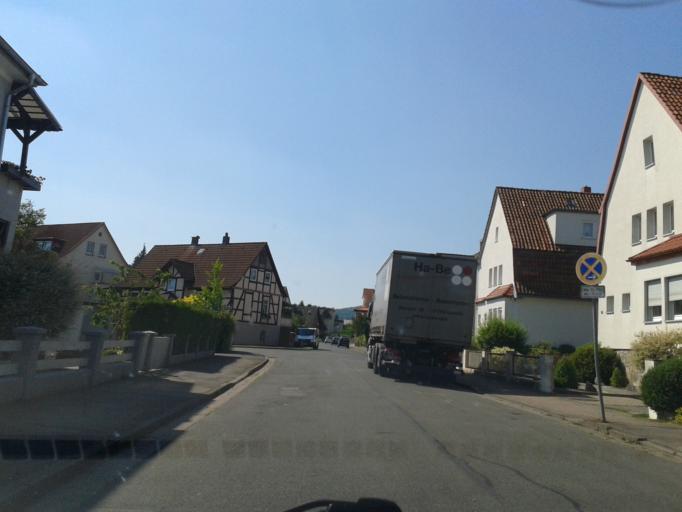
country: DE
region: Lower Saxony
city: Bad Pyrmont
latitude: 51.9820
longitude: 9.2428
